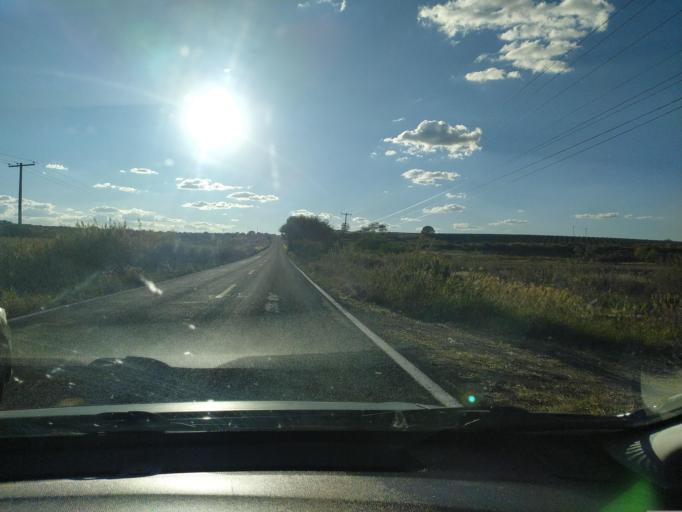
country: MX
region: Jalisco
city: San Diego de Alejandria
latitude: 21.0223
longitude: -101.9441
